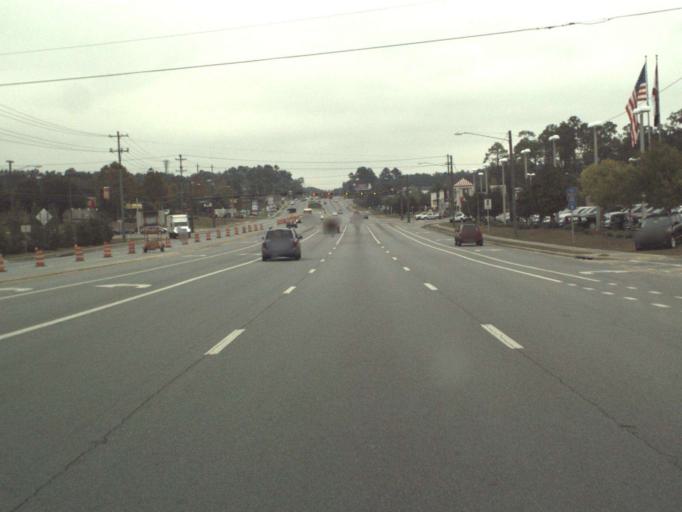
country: US
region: Florida
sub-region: Leon County
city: Tallahassee
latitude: 30.4570
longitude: -84.3609
